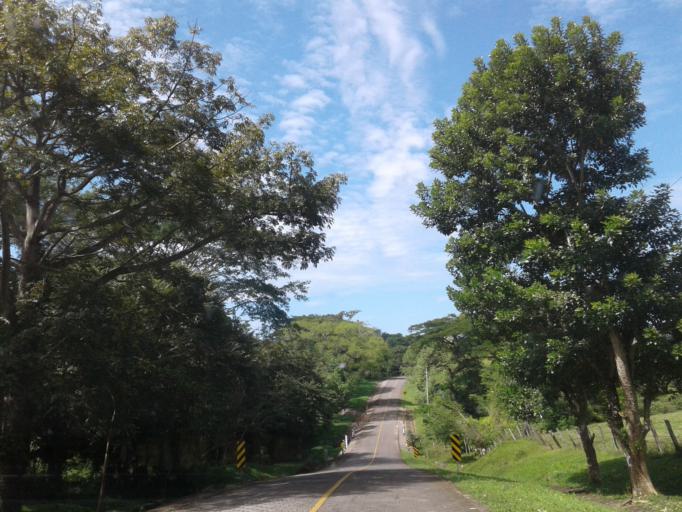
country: NI
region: Rivas
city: Cardenas
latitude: 11.1760
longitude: -85.4866
